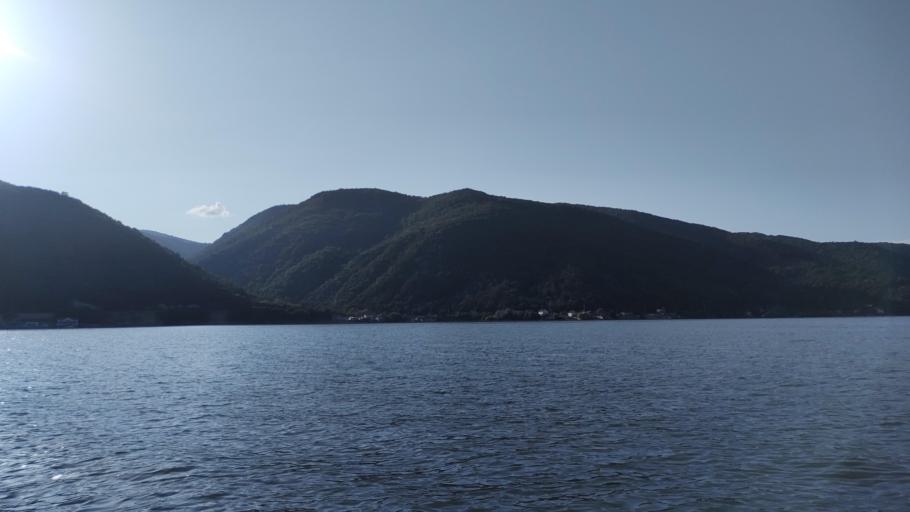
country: RO
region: Mehedinti
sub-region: Comuna Dubova
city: Dubova
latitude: 44.5668
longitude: 22.2379
